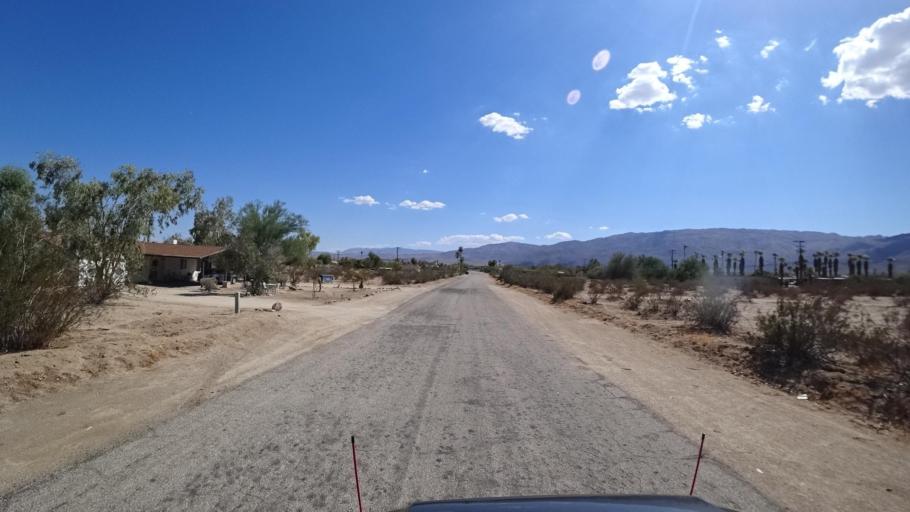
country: US
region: California
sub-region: San Diego County
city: Borrego Springs
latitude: 33.2470
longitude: -116.3726
